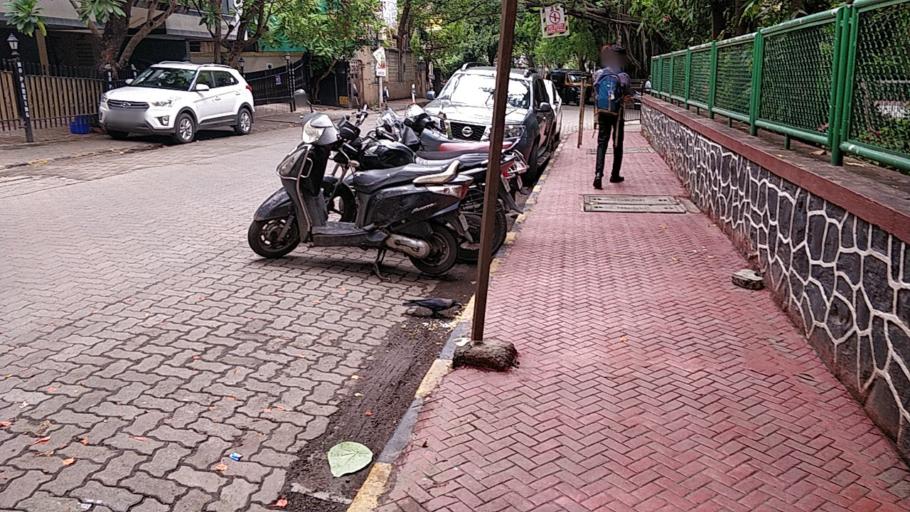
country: IN
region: Maharashtra
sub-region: Mumbai Suburban
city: Mumbai
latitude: 19.0634
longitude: 72.8330
